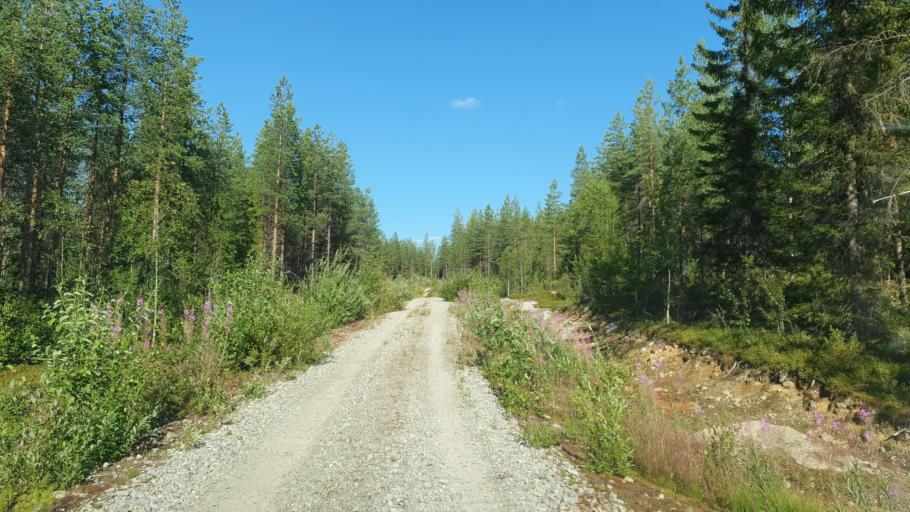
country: FI
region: Kainuu
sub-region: Kehys-Kainuu
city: Kuhmo
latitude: 64.0017
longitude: 29.7454
